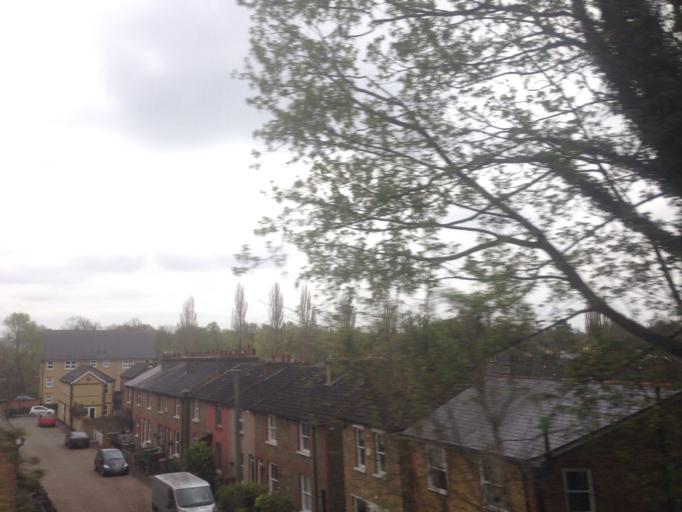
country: GB
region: England
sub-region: Greater London
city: Carshalton
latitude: 51.3697
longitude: -0.1627
